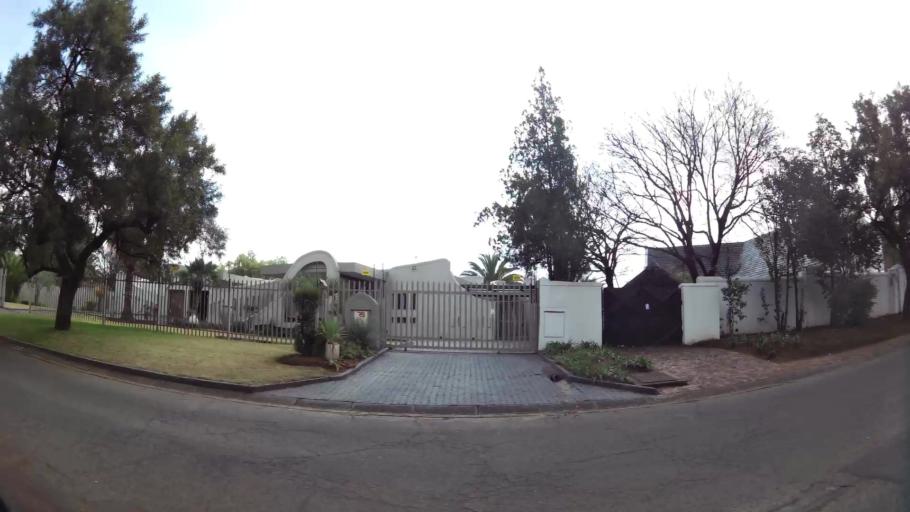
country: ZA
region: Gauteng
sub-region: Sedibeng District Municipality
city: Vanderbijlpark
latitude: -26.7398
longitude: 27.8262
